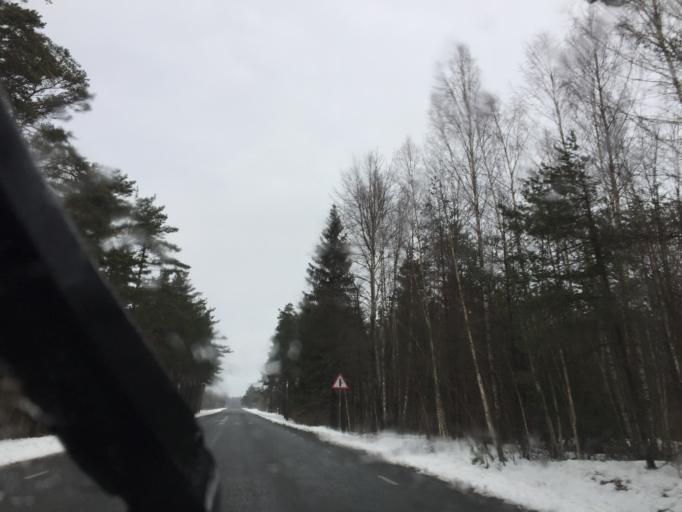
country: EE
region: Saare
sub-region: Kuressaare linn
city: Kuressaare
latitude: 58.3143
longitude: 22.0244
